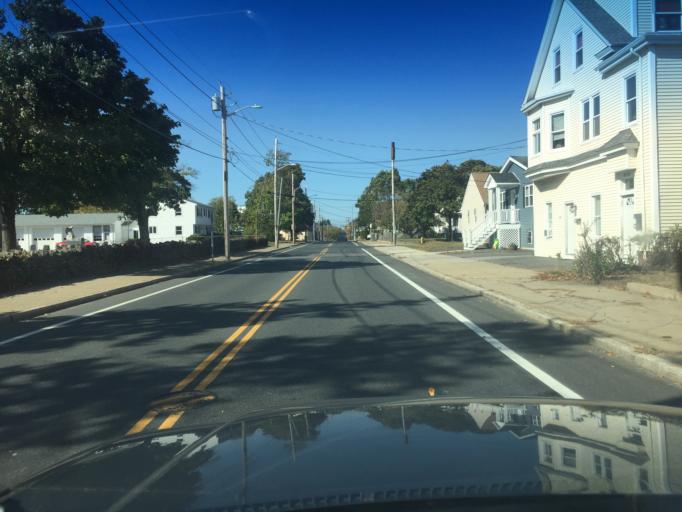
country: US
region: Rhode Island
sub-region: Providence County
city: Pawtucket
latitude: 41.8588
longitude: -71.3662
